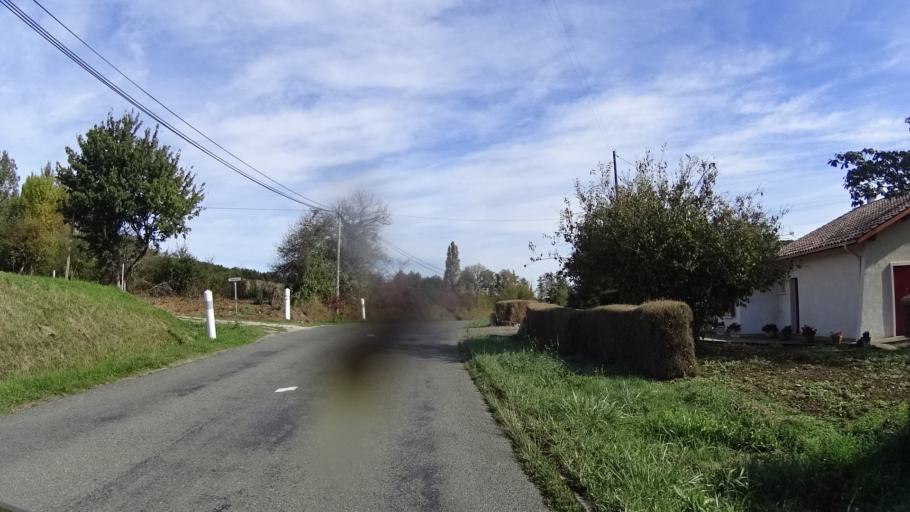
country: FR
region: Aquitaine
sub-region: Departement du Lot-et-Garonne
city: Castelculier
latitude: 44.1938
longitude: 0.7183
